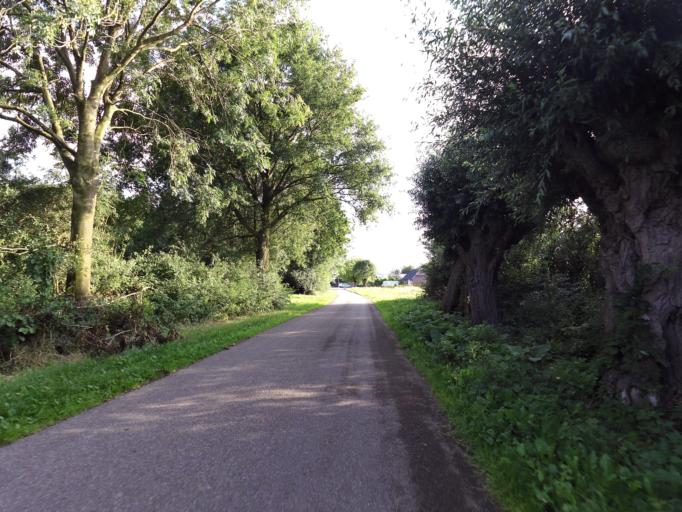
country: NL
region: Gelderland
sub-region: Gemeente Doesburg
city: Doesburg
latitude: 51.9881
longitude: 6.1171
